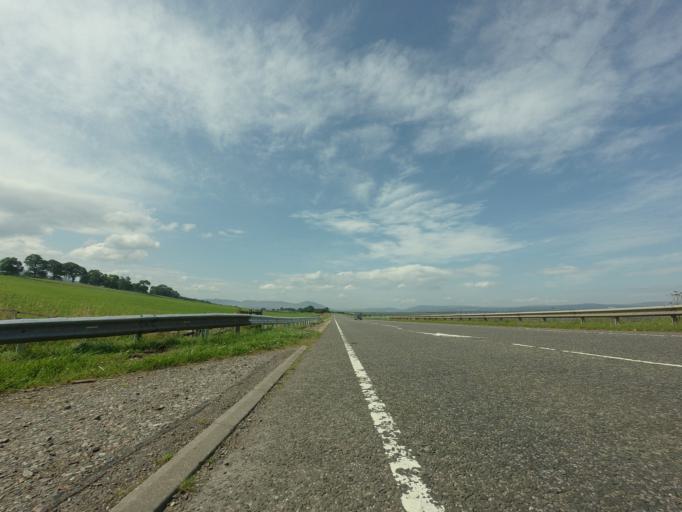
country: GB
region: Scotland
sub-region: Highland
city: Tain
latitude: 57.8294
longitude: -4.0863
